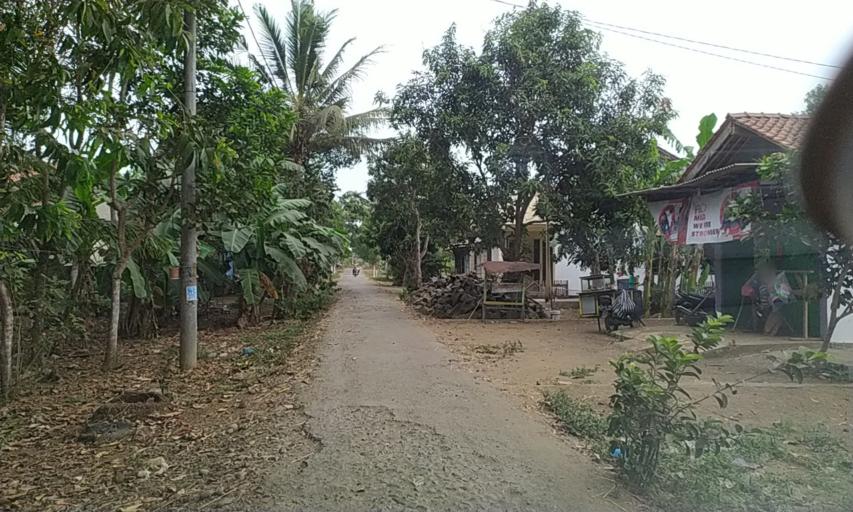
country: ID
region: Central Java
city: Kroya
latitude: -7.6911
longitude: 109.2664
